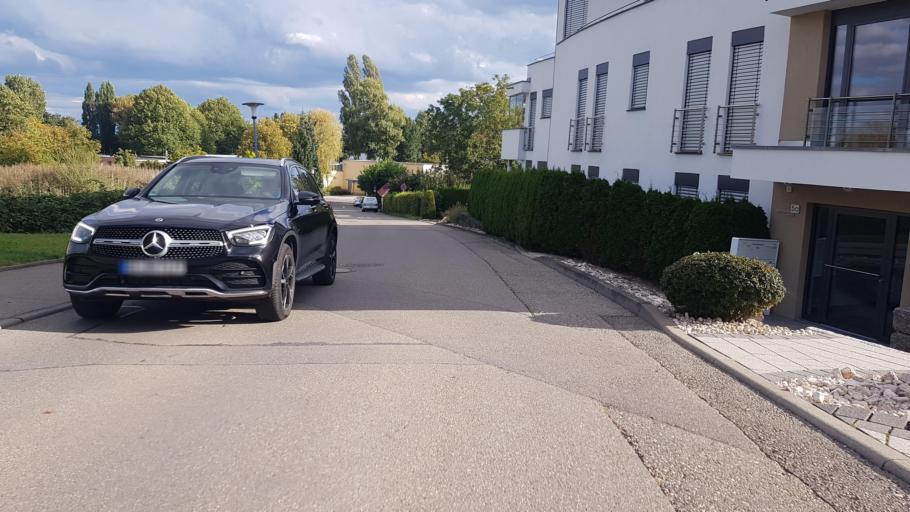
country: DE
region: Baden-Wuerttemberg
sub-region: Tuebingen Region
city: Immenstaad am Bodensee
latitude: 47.6620
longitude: 9.3546
